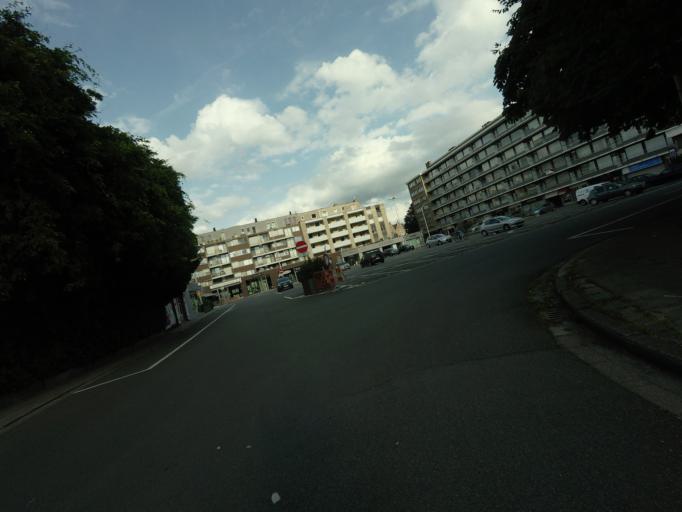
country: BE
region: Flanders
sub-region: Provincie Antwerpen
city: Aartselaar
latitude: 51.1718
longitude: 4.3927
